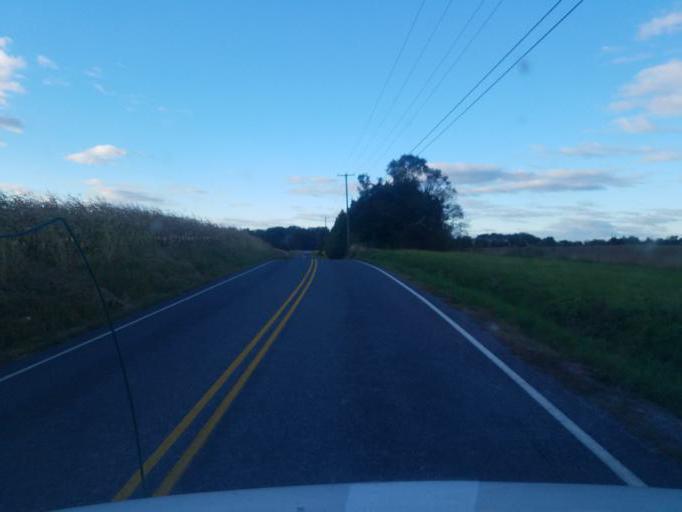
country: US
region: Pennsylvania
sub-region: Adams County
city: New Oxford
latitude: 39.9197
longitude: -77.0709
